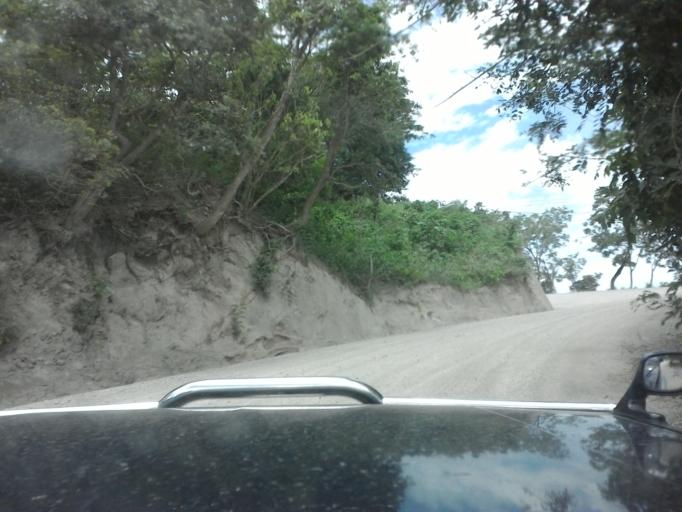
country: CR
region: Guanacaste
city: Juntas
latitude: 10.2403
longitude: -84.8514
